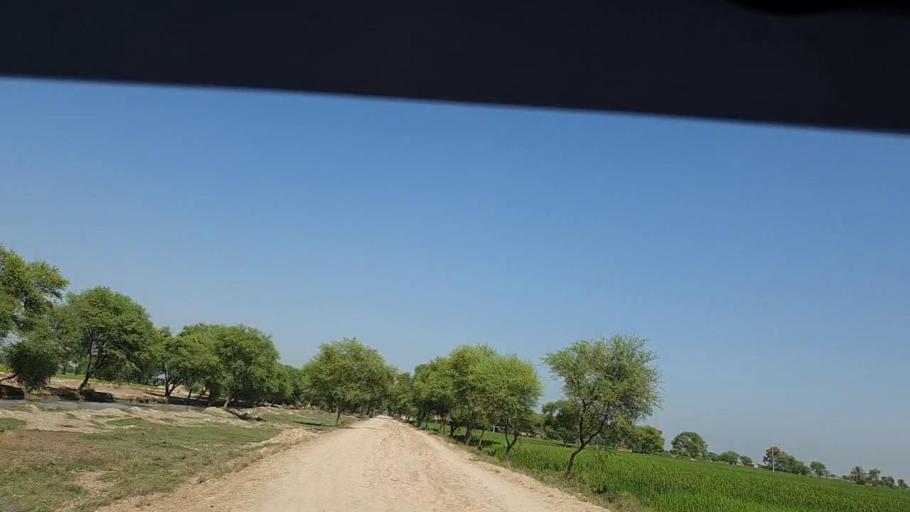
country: PK
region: Sindh
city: Tangwani
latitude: 28.2948
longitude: 69.0943
